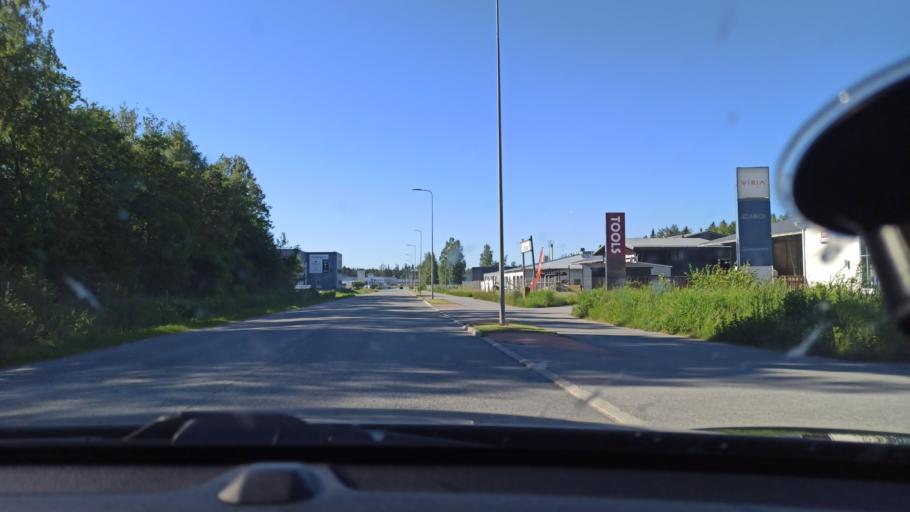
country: FI
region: Ostrobothnia
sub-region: Jakobstadsregionen
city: Jakobstad
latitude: 63.6852
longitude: 22.7112
